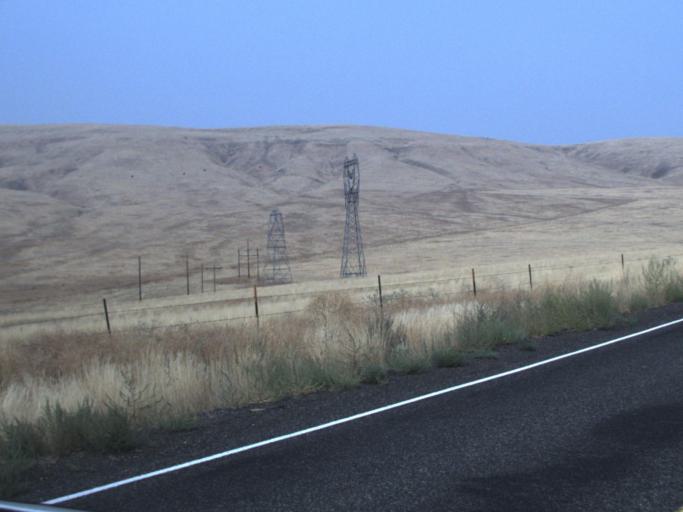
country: US
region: Washington
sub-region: Yakima County
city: Sunnyside
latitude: 46.4677
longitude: -119.9336
